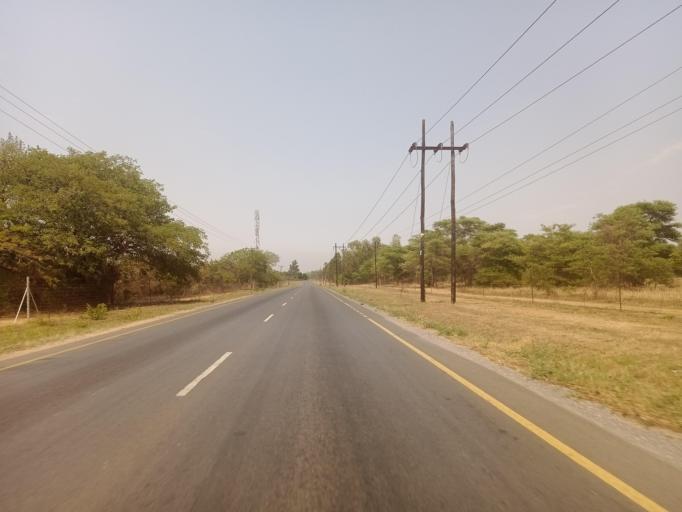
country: ZM
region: Lusaka
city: Lusaka
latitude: -15.2849
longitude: 28.3837
